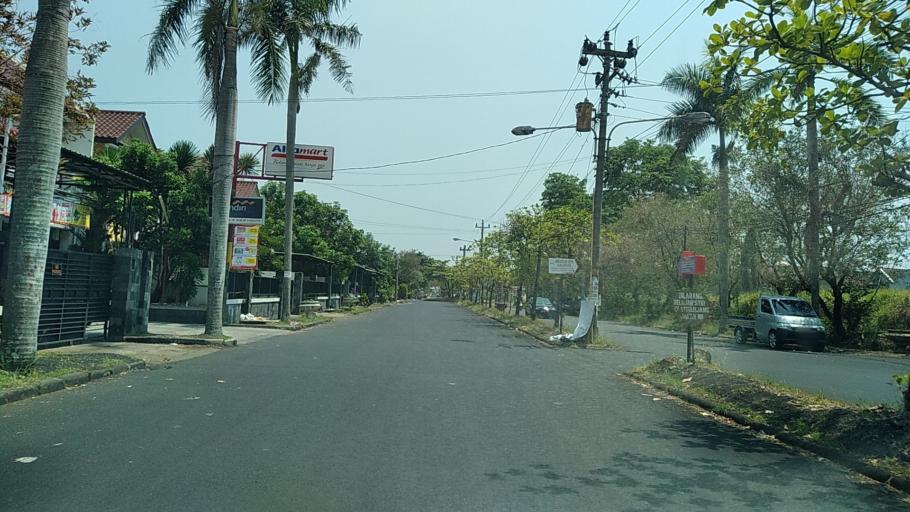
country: ID
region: Central Java
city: Mranggen
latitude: -7.0122
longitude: 110.4828
